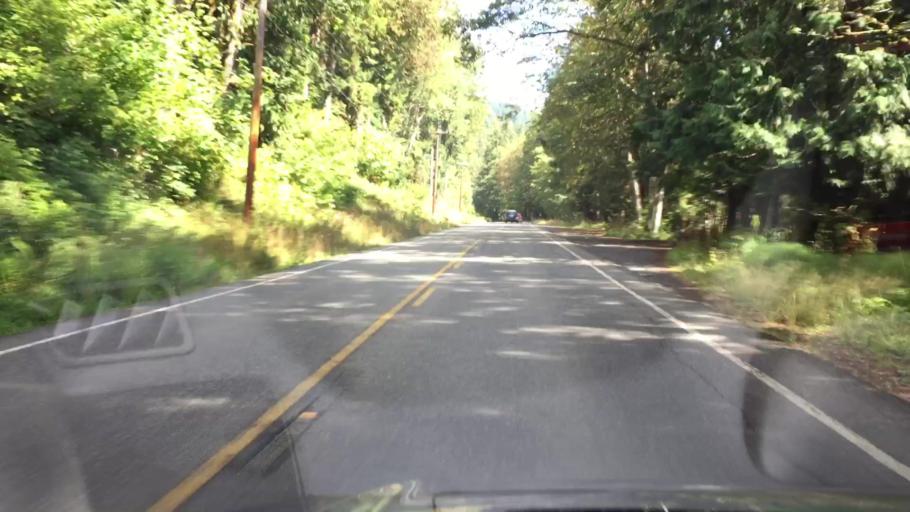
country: US
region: Washington
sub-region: Pierce County
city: Eatonville
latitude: 46.7556
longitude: -121.9559
